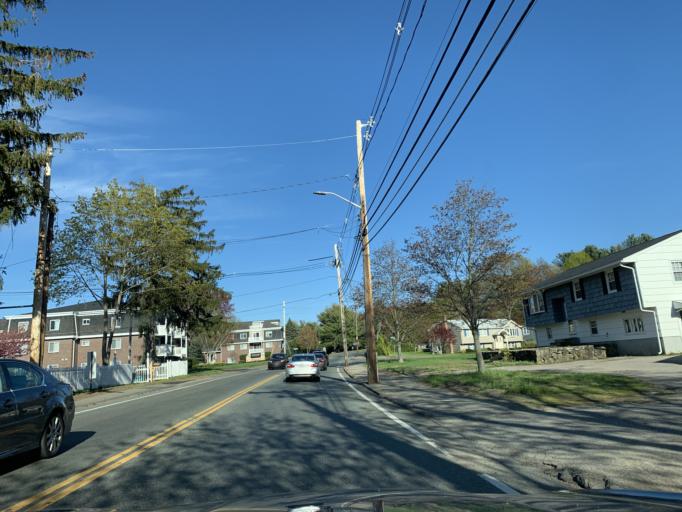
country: US
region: Massachusetts
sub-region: Norfolk County
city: Canton
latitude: 42.1338
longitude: -71.1391
